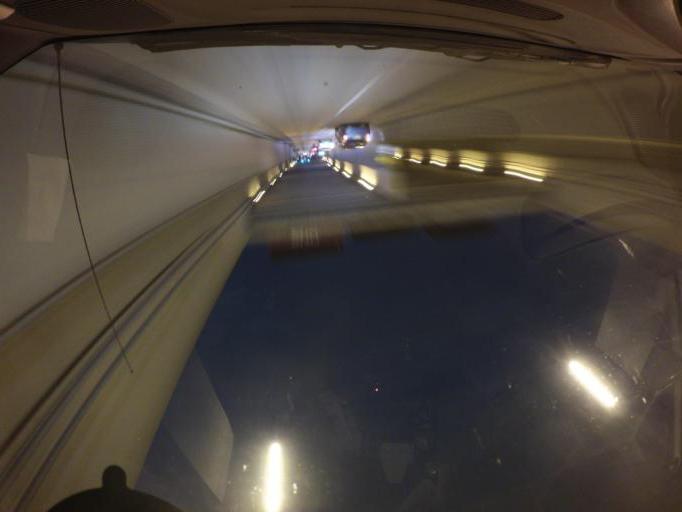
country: US
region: Illinois
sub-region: Cook County
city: Harvey
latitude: 41.6009
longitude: -87.6460
